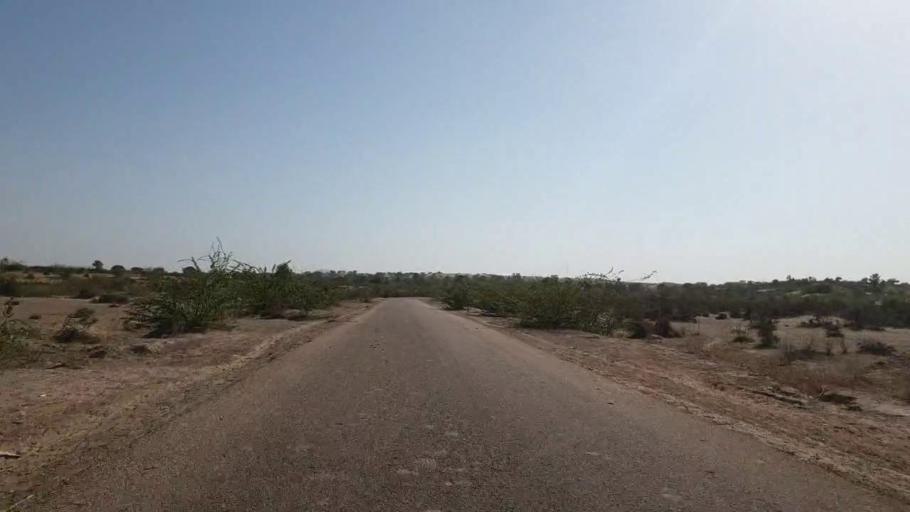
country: PK
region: Sindh
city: Islamkot
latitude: 25.0663
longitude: 70.0408
